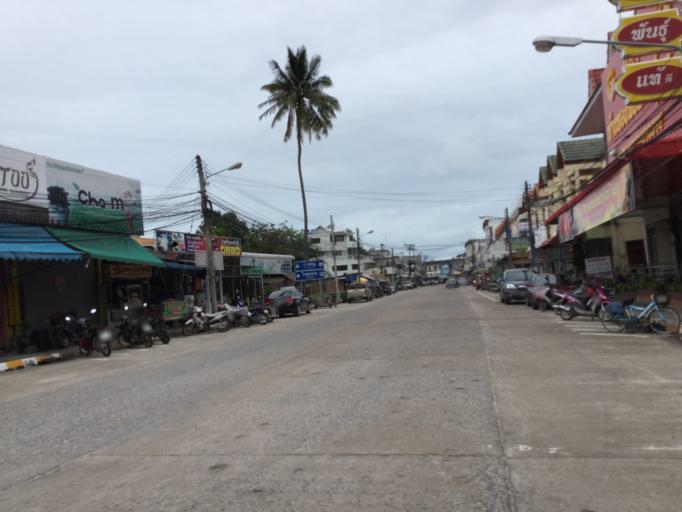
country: TH
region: Surat Thani
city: Ko Pha-Ngan
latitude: 9.7108
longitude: 99.9911
